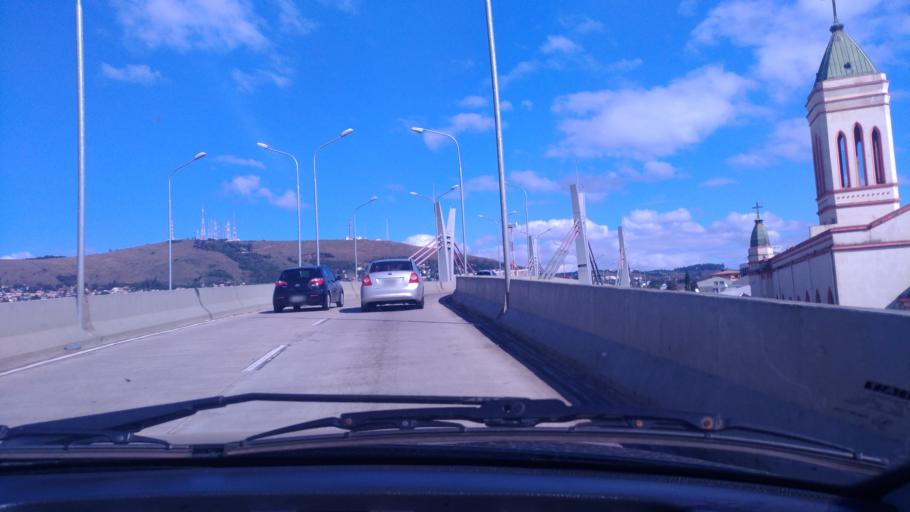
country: BR
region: Rio Grande do Sul
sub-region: Porto Alegre
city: Porto Alegre
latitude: -30.0626
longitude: -51.1852
